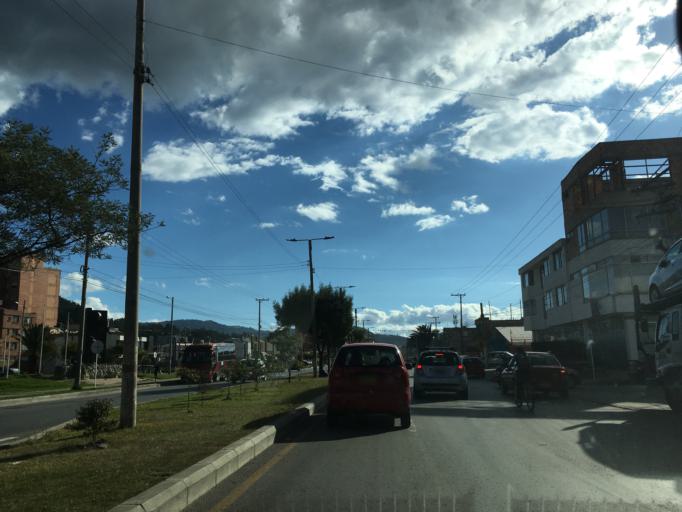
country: CO
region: Boyaca
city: Sogamoso
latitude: 5.7309
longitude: -72.9200
